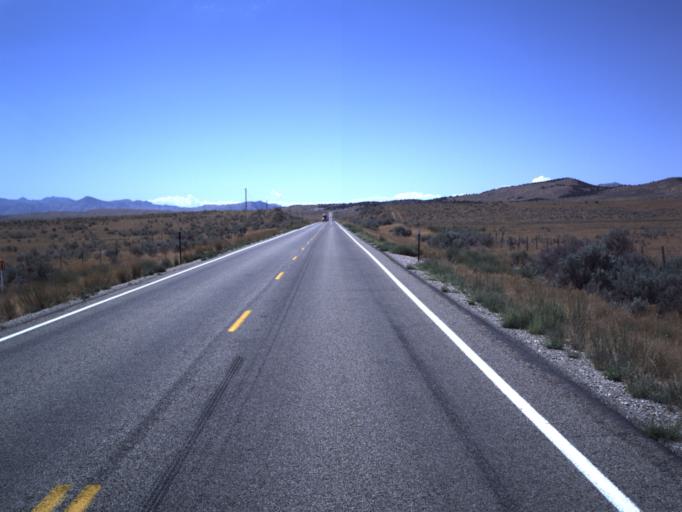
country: US
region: Utah
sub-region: Juab County
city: Nephi
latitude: 39.6860
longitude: -112.0066
